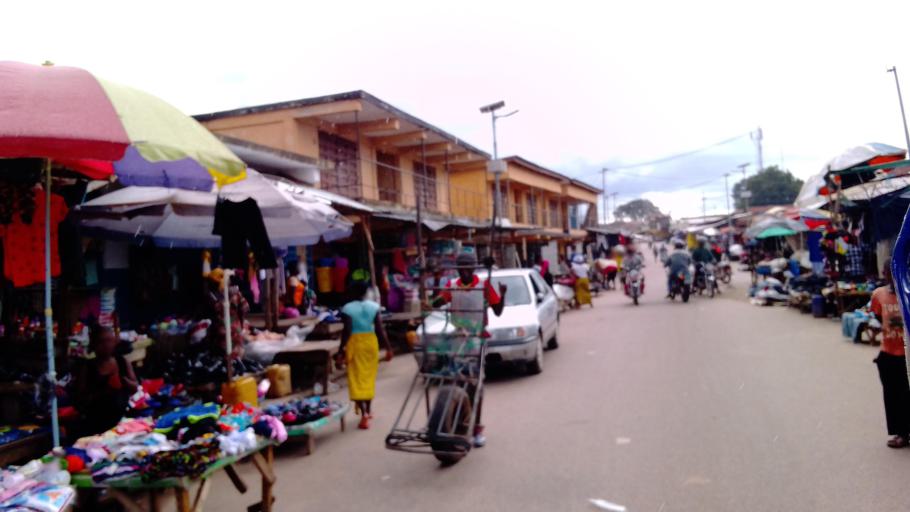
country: SL
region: Eastern Province
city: Koidu
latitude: 8.6457
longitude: -10.9728
